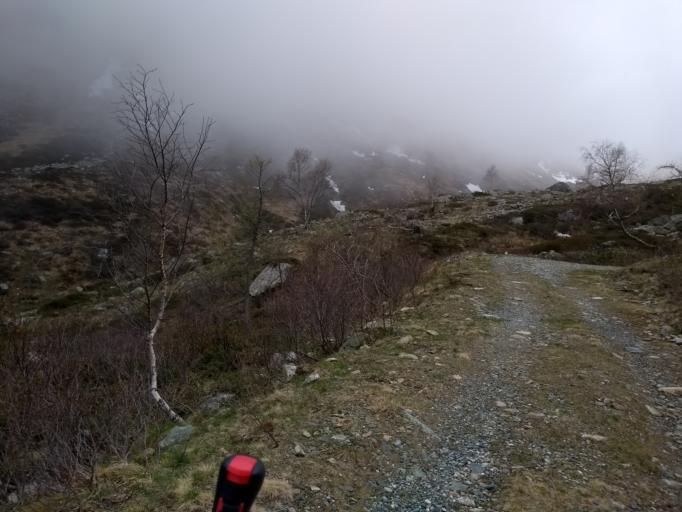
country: IT
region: Piedmont
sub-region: Provincia di Torino
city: Ala di Stura
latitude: 45.2866
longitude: 7.3408
